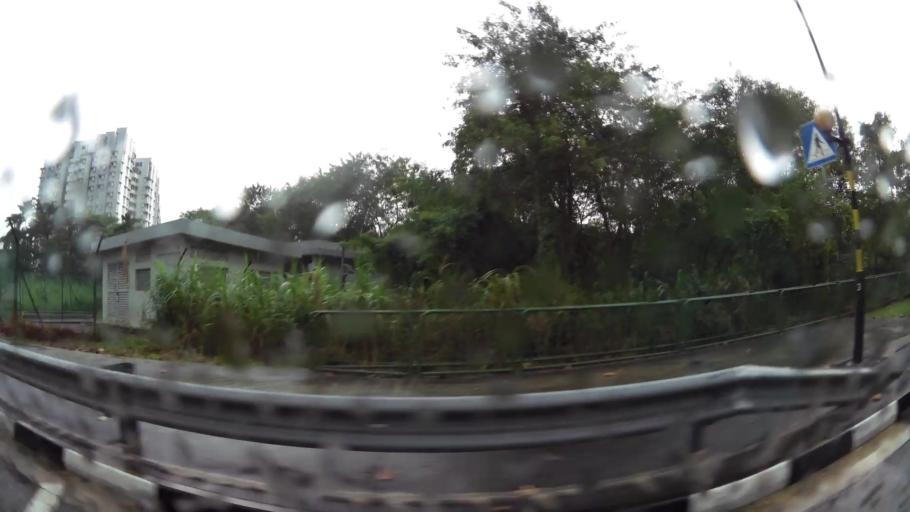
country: MY
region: Johor
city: Kampung Pasir Gudang Baru
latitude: 1.3936
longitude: 103.8345
